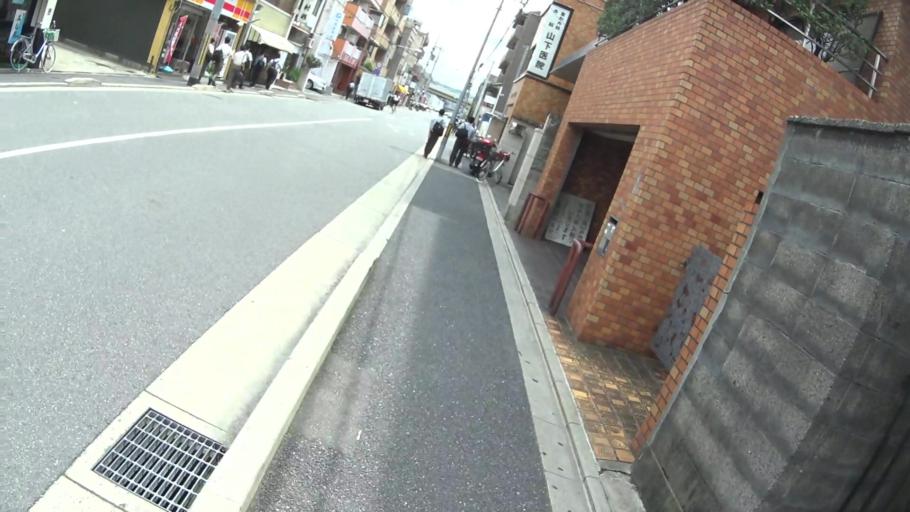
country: JP
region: Kyoto
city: Kyoto
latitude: 34.9842
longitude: 135.7477
